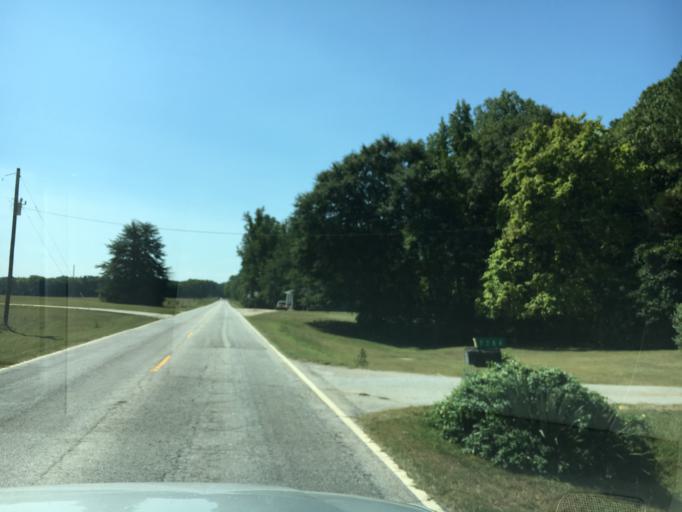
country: US
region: South Carolina
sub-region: Laurens County
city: Joanna
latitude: 34.2990
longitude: -81.8441
